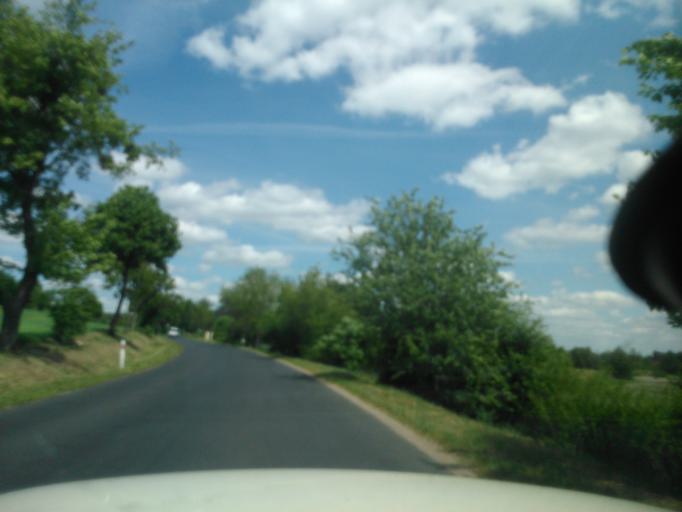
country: PL
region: Kujawsko-Pomorskie
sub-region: Powiat golubsko-dobrzynski
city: Golub-Dobrzyn
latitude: 53.1034
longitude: 19.0232
